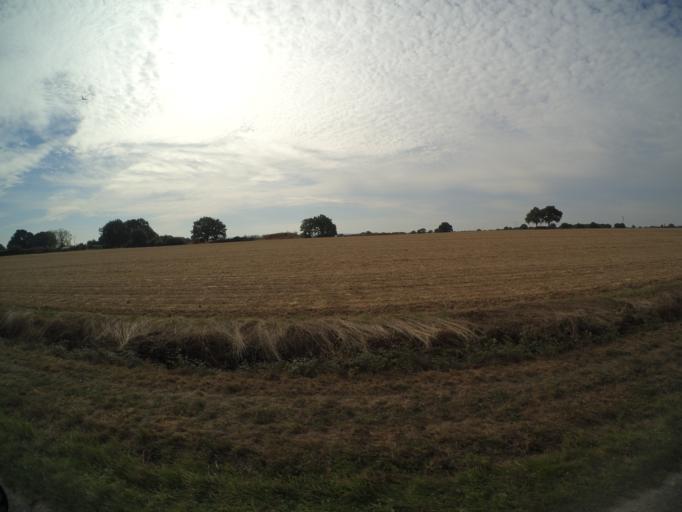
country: FR
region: Pays de la Loire
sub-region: Departement de Maine-et-Loire
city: Chemille-Melay
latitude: 47.2117
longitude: -0.7557
